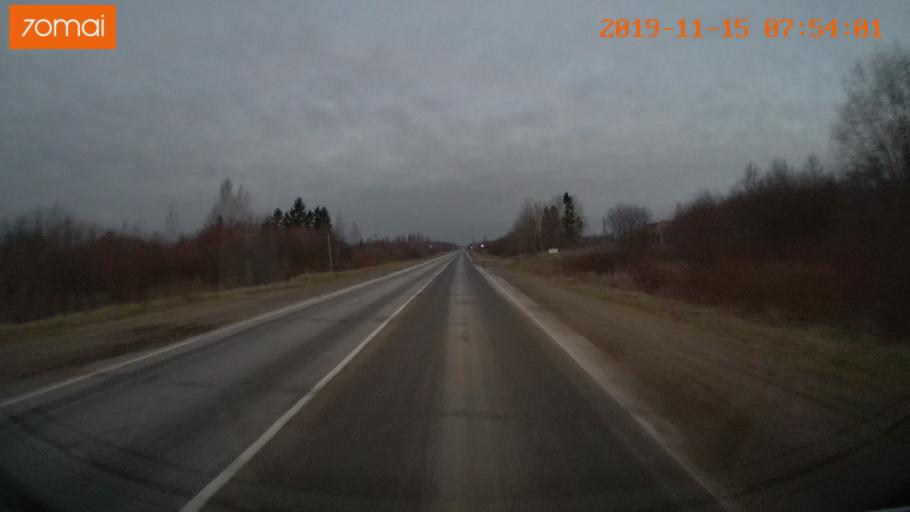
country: RU
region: Vologda
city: Cherepovets
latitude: 58.8946
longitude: 38.1806
